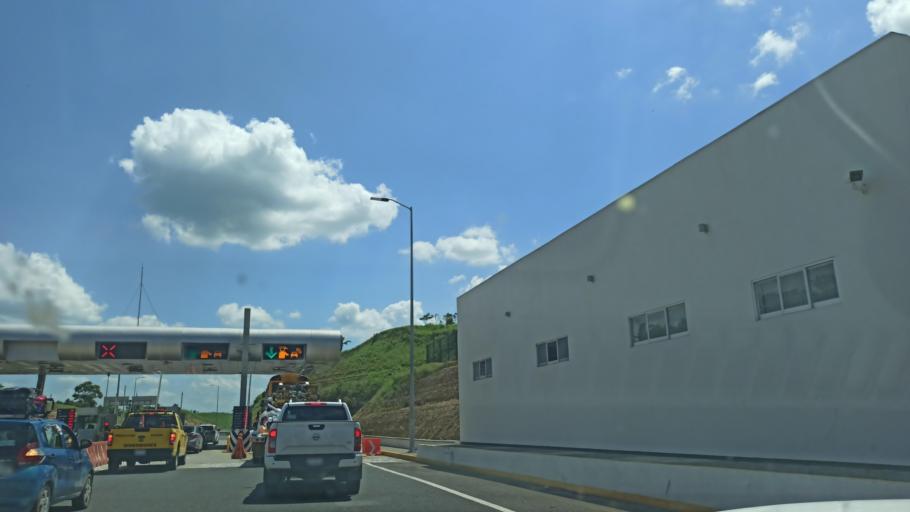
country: MX
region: Veracruz
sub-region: Papantla
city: Polutla
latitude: 20.4597
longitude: -97.2468
